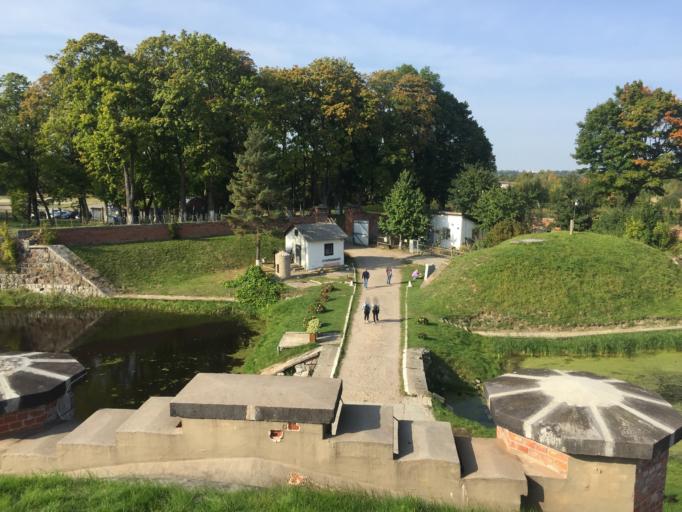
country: RU
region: Kaliningrad
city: Bol'shoe Isakovo
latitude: 54.6570
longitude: 20.5674
